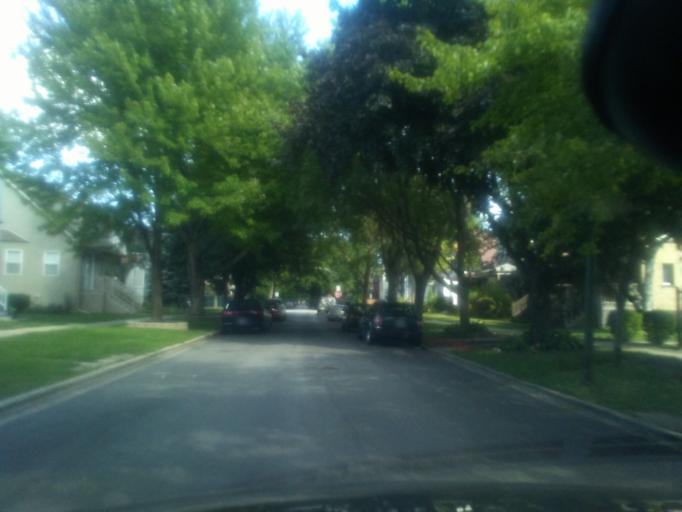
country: US
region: Illinois
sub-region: Cook County
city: Harwood Heights
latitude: 41.9656
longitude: -87.7661
